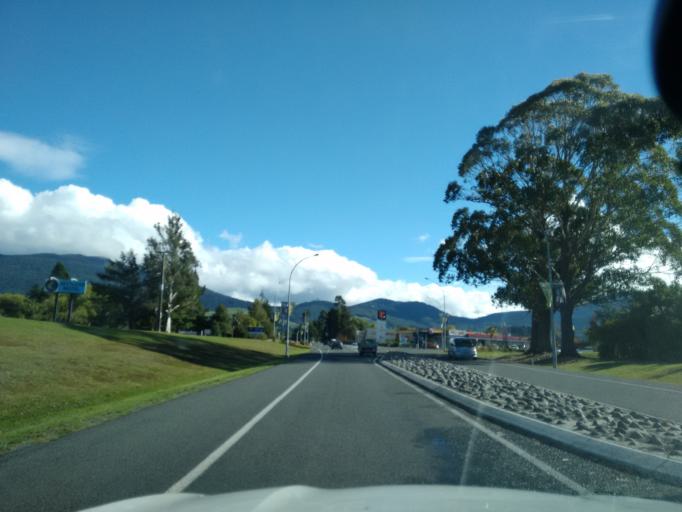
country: NZ
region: Waikato
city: Turangi
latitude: -38.9901
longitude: 175.8121
